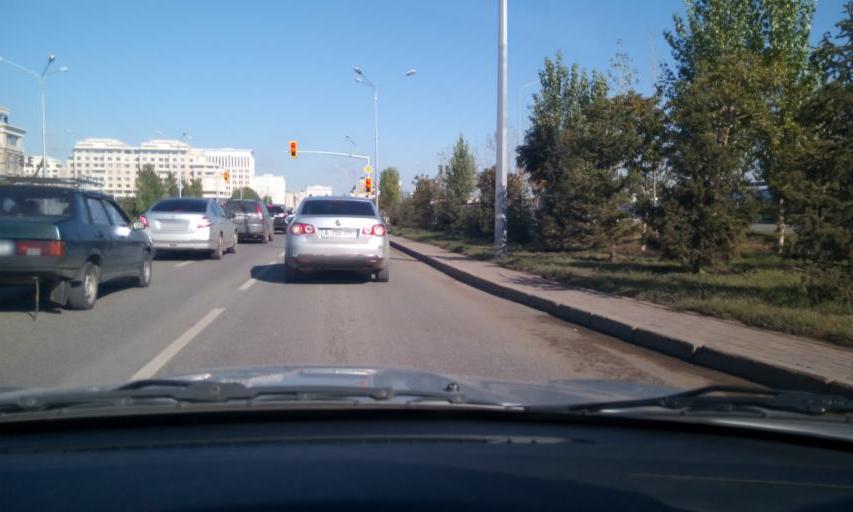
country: KZ
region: Astana Qalasy
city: Astana
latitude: 51.0992
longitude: 71.4284
